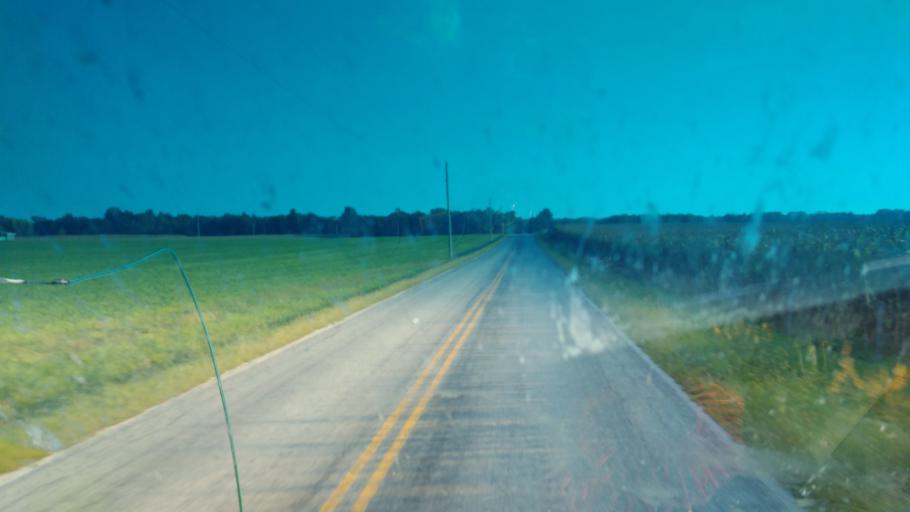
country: US
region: Ohio
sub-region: Crawford County
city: Bucyrus
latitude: 40.8473
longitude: -82.8730
